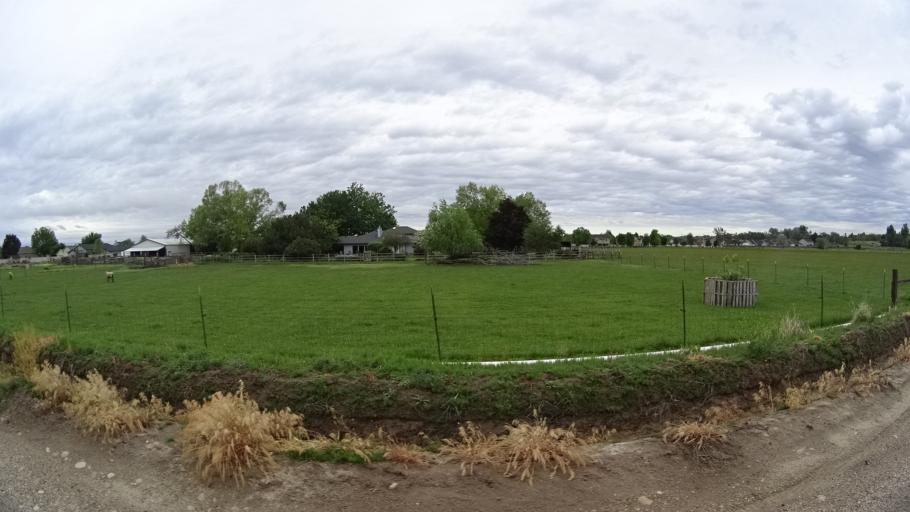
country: US
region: Idaho
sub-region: Ada County
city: Star
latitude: 43.7048
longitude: -116.4734
